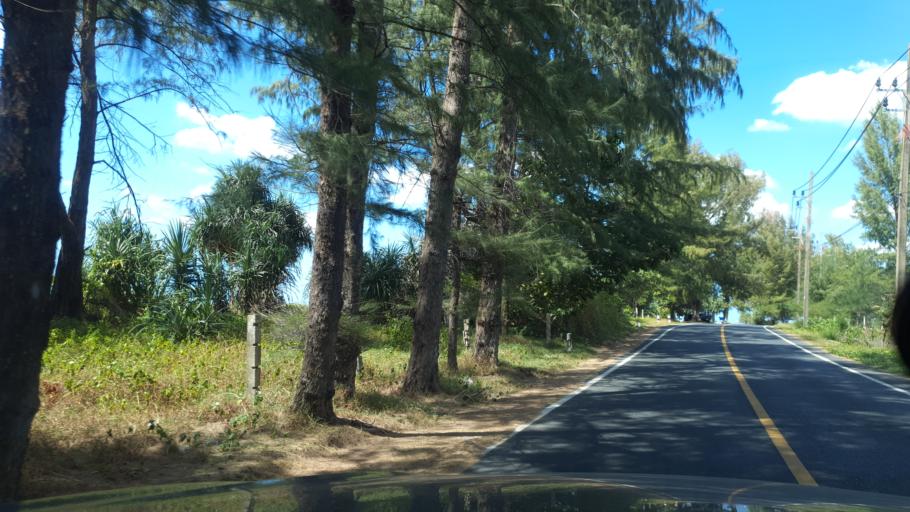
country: TH
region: Phangnga
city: Thai Mueang
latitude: 8.2946
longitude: 98.2724
